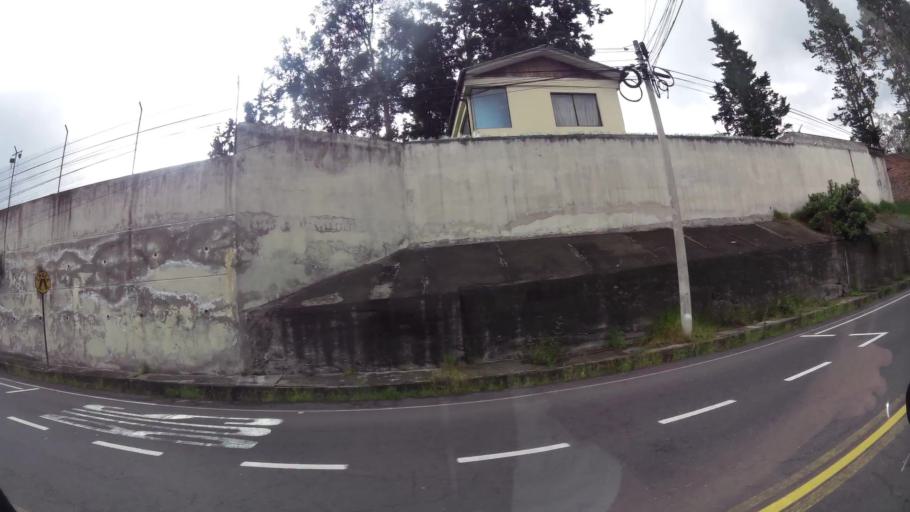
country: EC
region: Pichincha
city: Sangolqui
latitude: -0.3432
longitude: -78.4527
